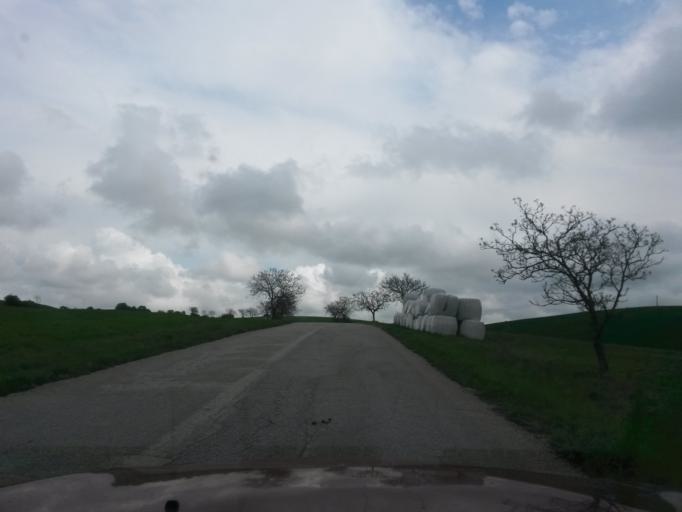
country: SK
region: Kosicky
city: Roznava
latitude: 48.5611
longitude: 20.4882
